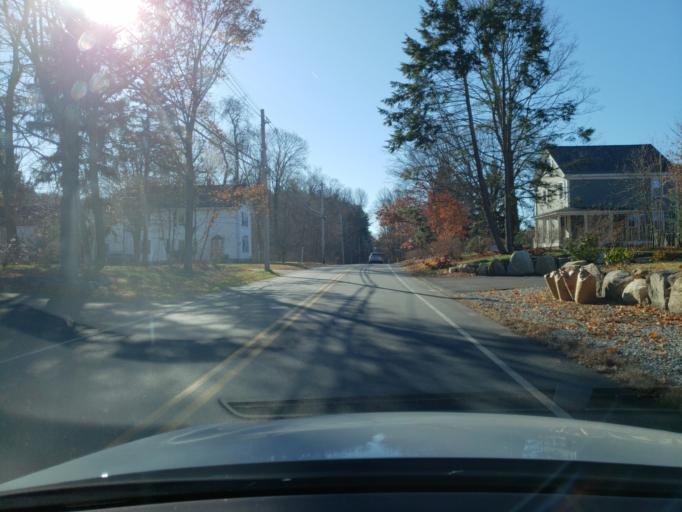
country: US
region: Massachusetts
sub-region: Essex County
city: Andover
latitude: 42.6719
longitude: -71.1365
